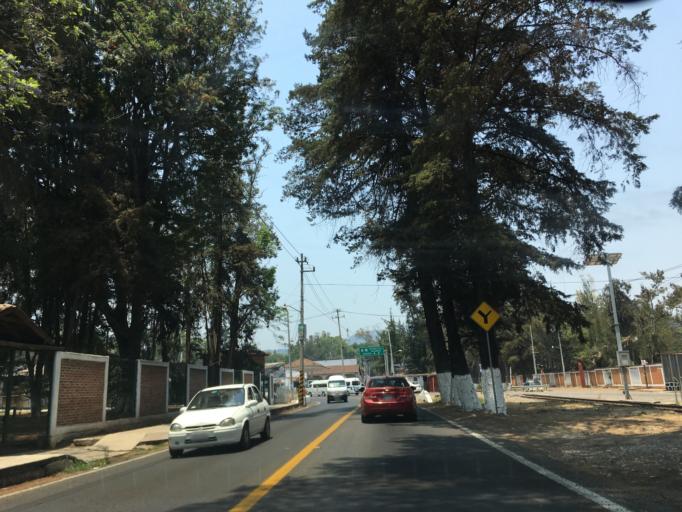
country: MX
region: Michoacan
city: Patzcuaro
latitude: 19.5405
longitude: -101.6115
